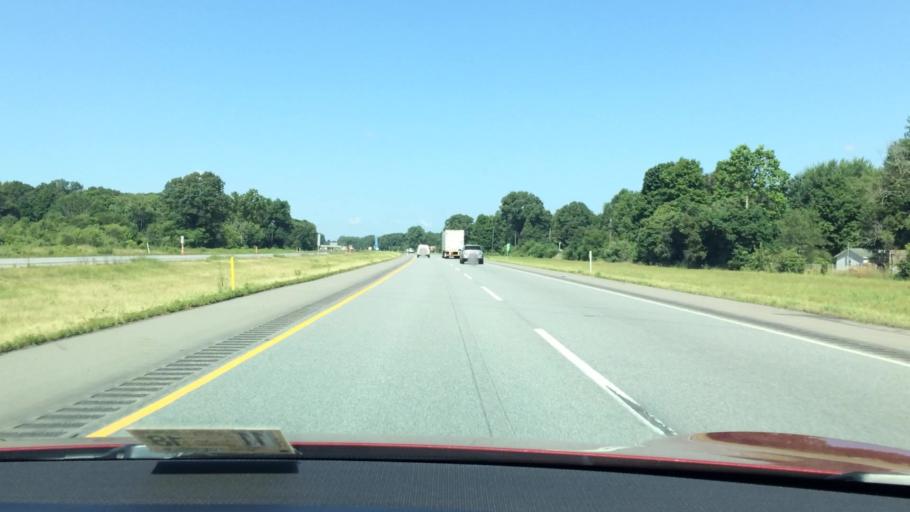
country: US
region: Indiana
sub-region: Elkhart County
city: Simonton Lake
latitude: 41.7330
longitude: -86.0242
